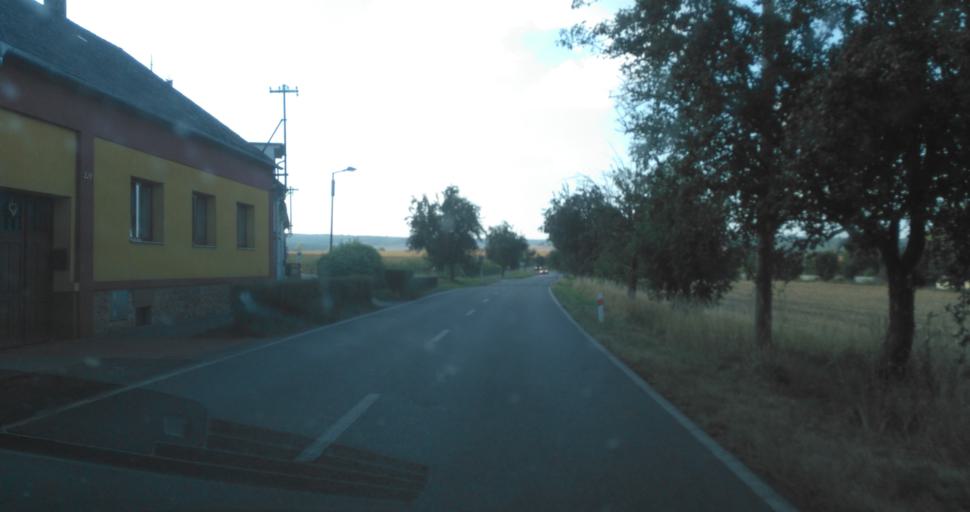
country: CZ
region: Central Bohemia
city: Zebrak
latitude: 49.8781
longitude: 13.8901
